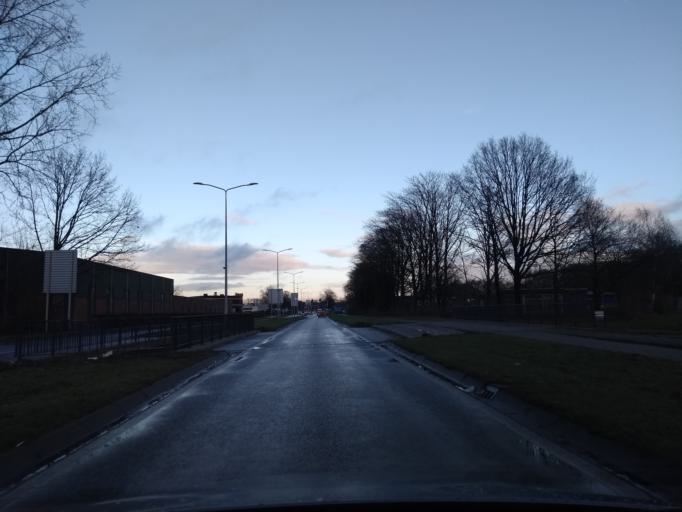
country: NL
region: Overijssel
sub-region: Gemeente Almelo
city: Almelo
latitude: 52.3715
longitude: 6.6469
